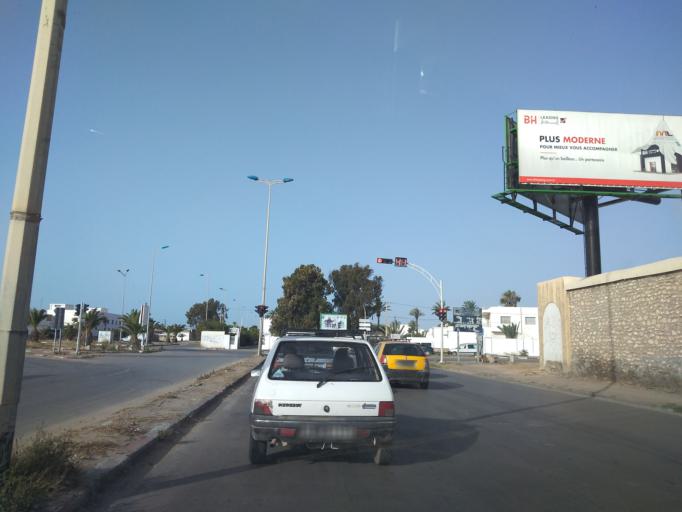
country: TN
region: Safaqis
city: Sfax
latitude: 34.7318
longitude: 10.7465
